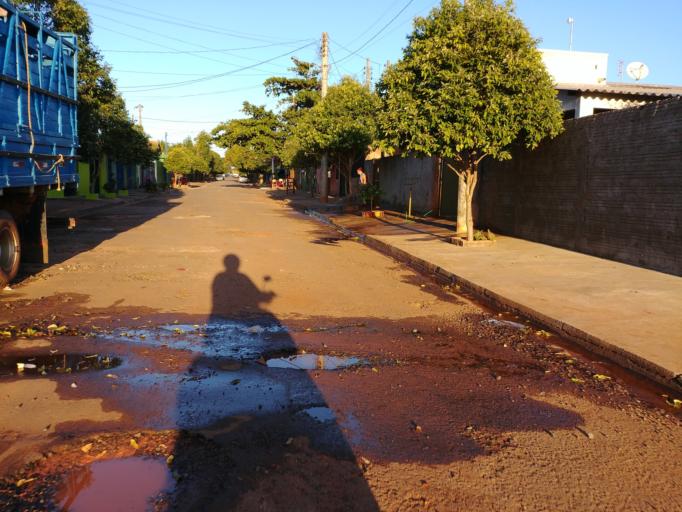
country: BR
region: Sao Paulo
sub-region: Paraguacu Paulista
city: Paraguacu Paulista
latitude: -22.4268
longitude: -50.5899
